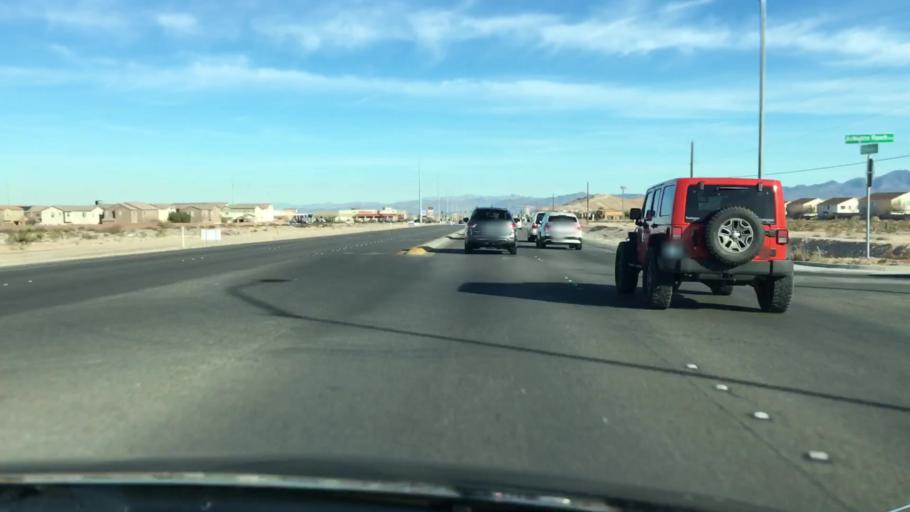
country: US
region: Nevada
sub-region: Clark County
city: Enterprise
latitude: 36.0203
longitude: -115.2853
